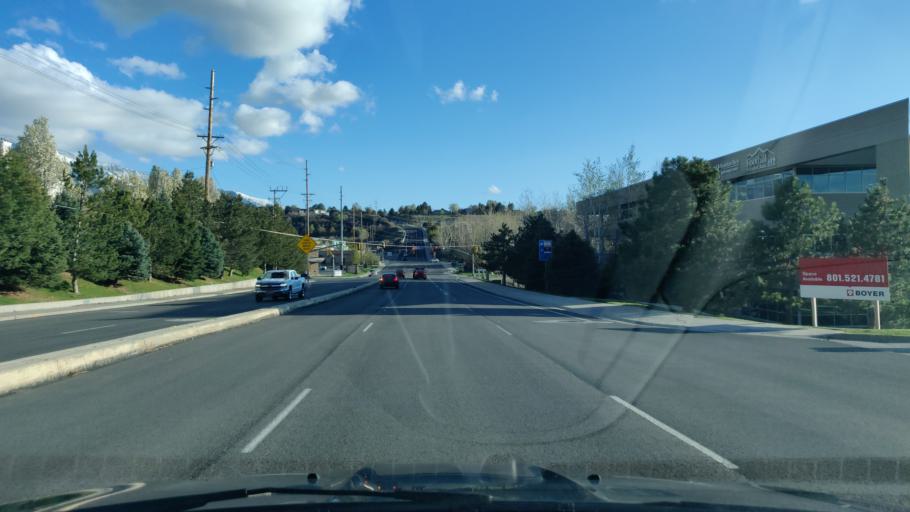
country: US
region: Utah
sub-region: Salt Lake County
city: Cottonwood Heights
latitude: 40.6346
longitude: -111.8061
